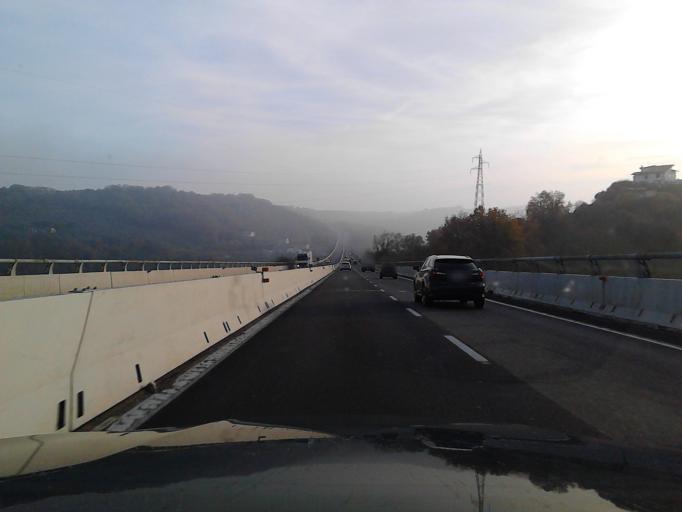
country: IT
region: Abruzzo
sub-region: Provincia di Chieti
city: San Vito Chietino
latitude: 42.2940
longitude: 14.4330
